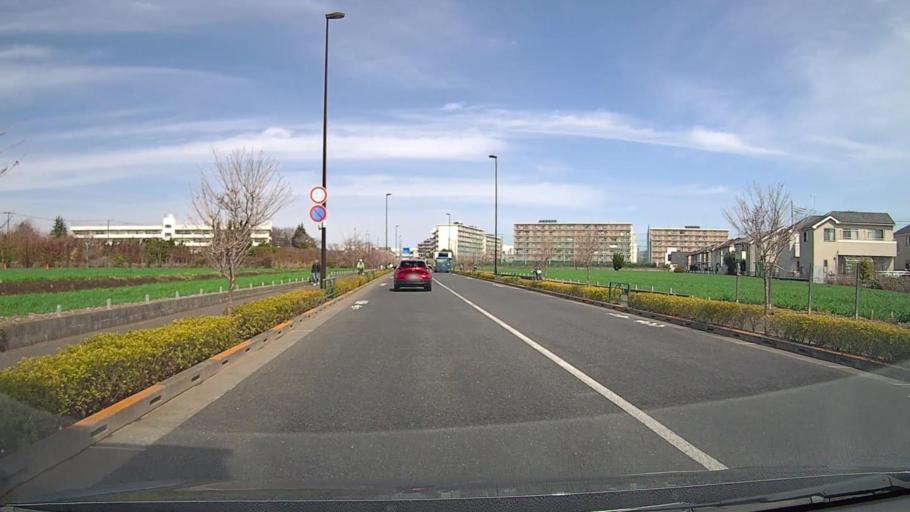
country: JP
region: Tokyo
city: Tanashicho
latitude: 35.7384
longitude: 139.5249
